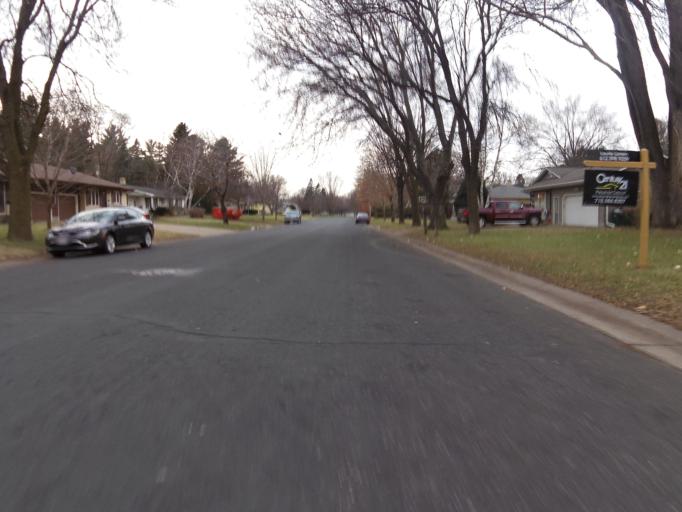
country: US
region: Wisconsin
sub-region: Pierce County
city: River Falls
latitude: 44.8559
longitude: -92.6116
